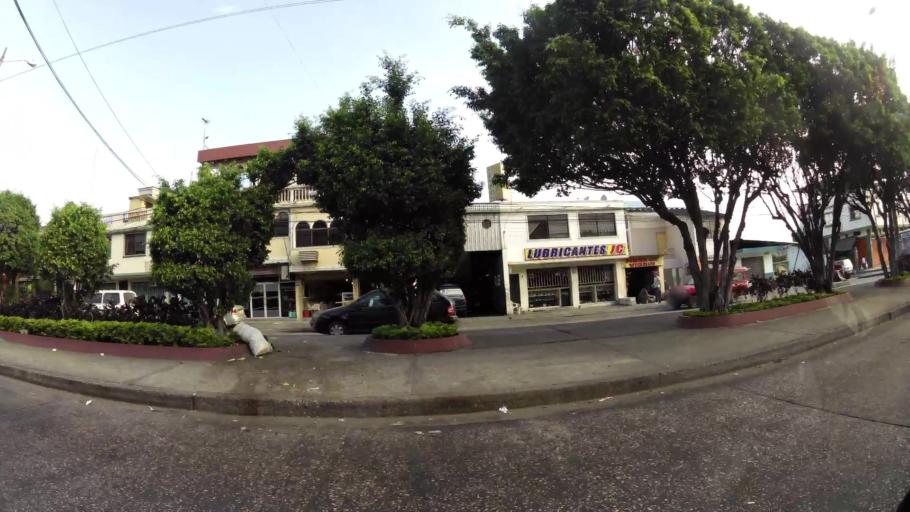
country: EC
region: Guayas
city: Eloy Alfaro
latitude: -2.1329
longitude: -79.9063
